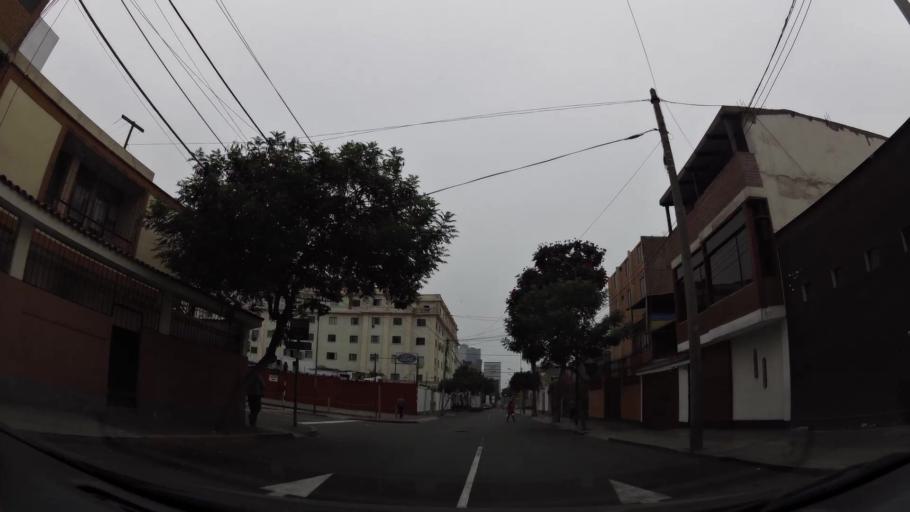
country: PE
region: Lima
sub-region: Lima
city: San Isidro
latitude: -12.1152
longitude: -77.0273
